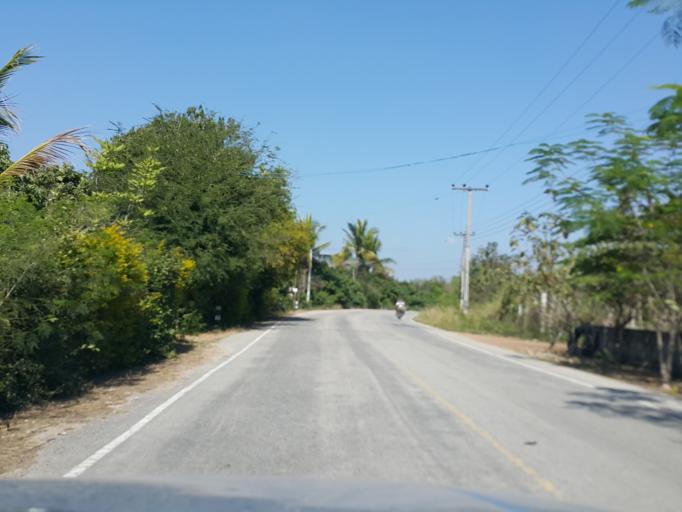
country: TH
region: Chiang Mai
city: Doi Lo
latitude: 18.5343
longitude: 98.7835
